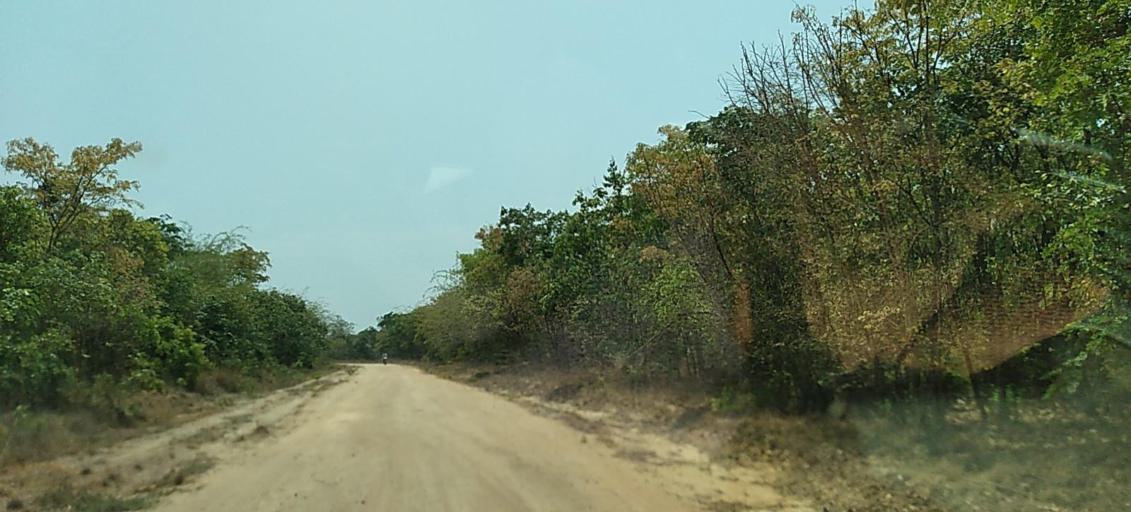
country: ZM
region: Copperbelt
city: Kalulushi
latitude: -12.9408
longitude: 28.1577
